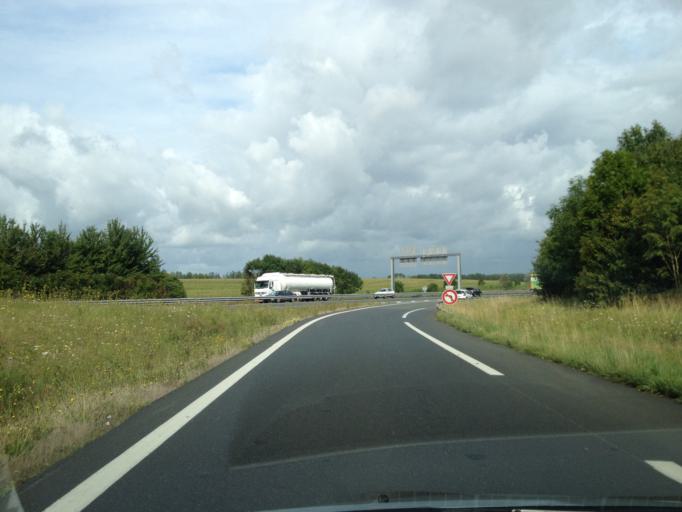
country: FR
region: Pays de la Loire
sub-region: Departement de la Vendee
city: Sainte-Hermine
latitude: 46.5386
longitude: -1.0795
